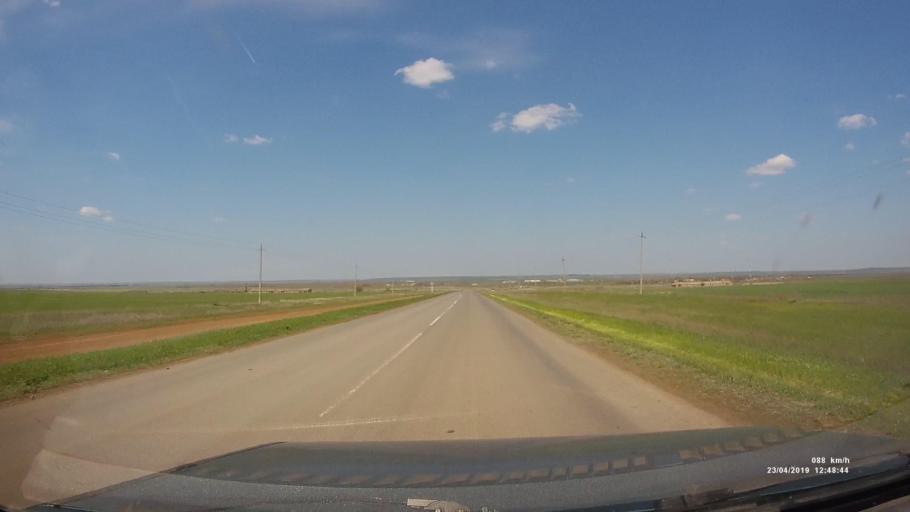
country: RU
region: Kalmykiya
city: Yashalta
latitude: 46.5283
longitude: 42.6389
